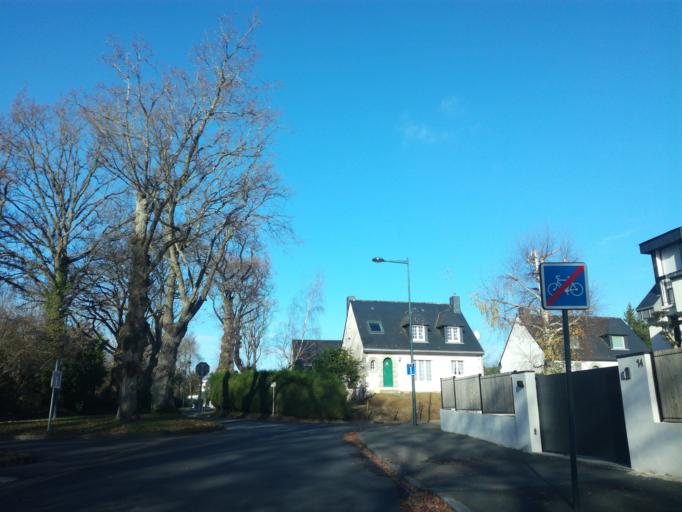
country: FR
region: Brittany
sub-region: Departement d'Ille-et-Vilaine
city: Chantepie
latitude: 48.0911
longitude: -1.6101
